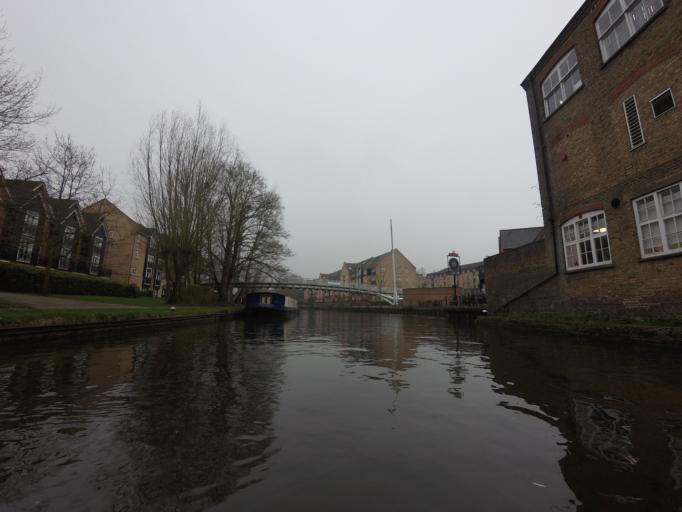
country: GB
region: England
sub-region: Hertfordshire
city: Kings Langley
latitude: 51.7341
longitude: -0.4615
